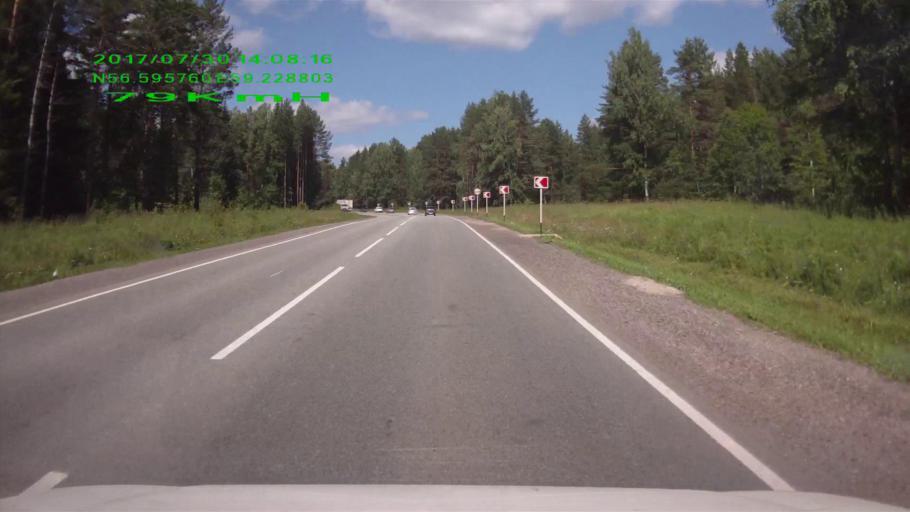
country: RU
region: Sverdlovsk
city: Nizhniye Sergi
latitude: 56.5964
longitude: 59.2291
